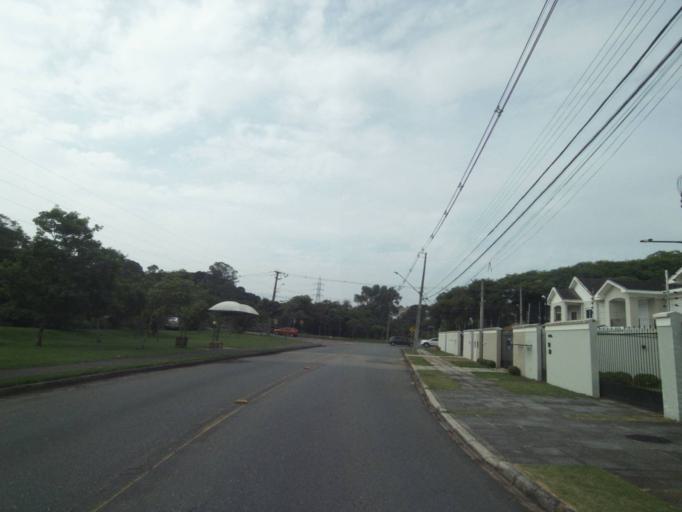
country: BR
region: Parana
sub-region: Curitiba
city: Curitiba
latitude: -25.4051
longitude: -49.3029
